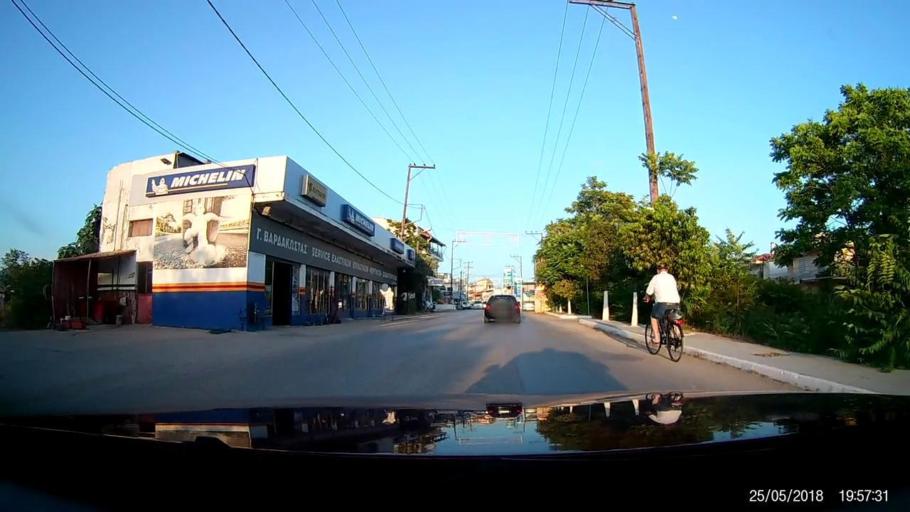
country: GR
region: Central Greece
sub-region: Nomos Evvoias
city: Vasilikon
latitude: 38.4263
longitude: 23.6675
